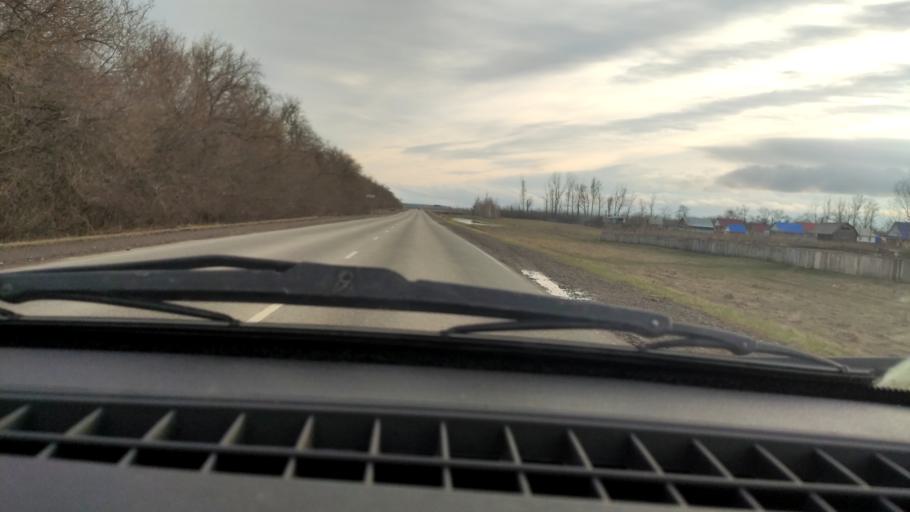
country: RU
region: Bashkortostan
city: Davlekanovo
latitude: 54.2905
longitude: 55.1202
